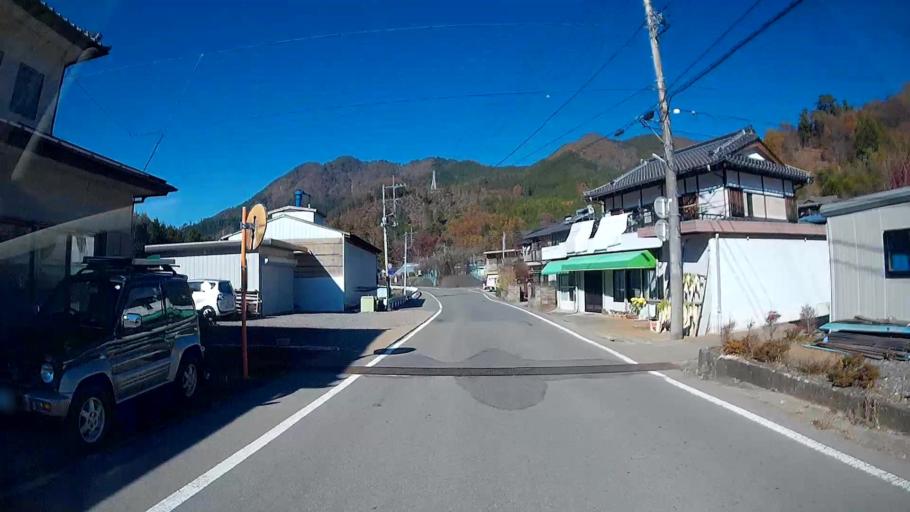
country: JP
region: Yamanashi
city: Otsuki
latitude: 35.5619
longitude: 138.9753
